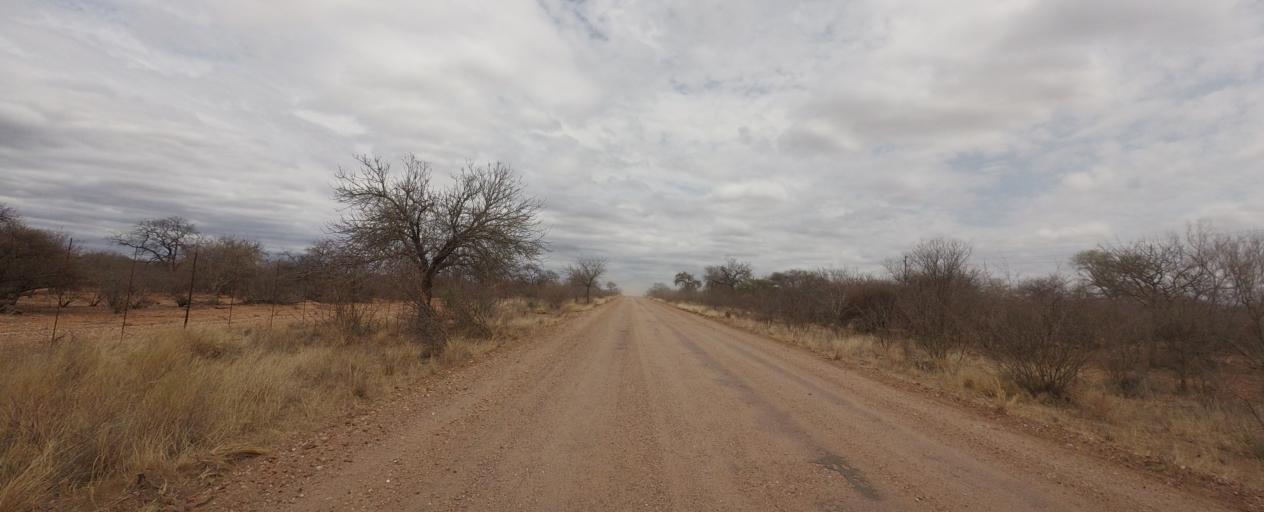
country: BW
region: Central
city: Mathathane
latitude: -22.6768
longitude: 28.6689
